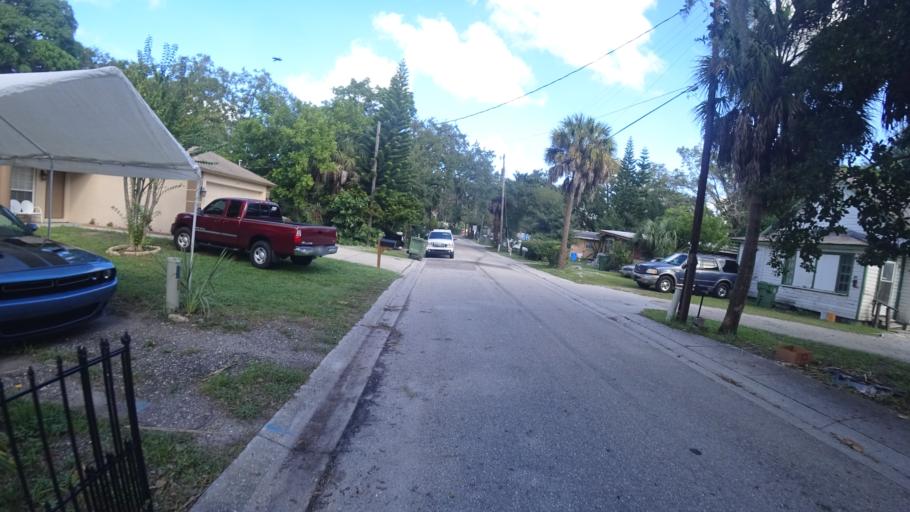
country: US
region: Florida
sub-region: Manatee County
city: Bradenton
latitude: 27.4889
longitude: -82.5584
